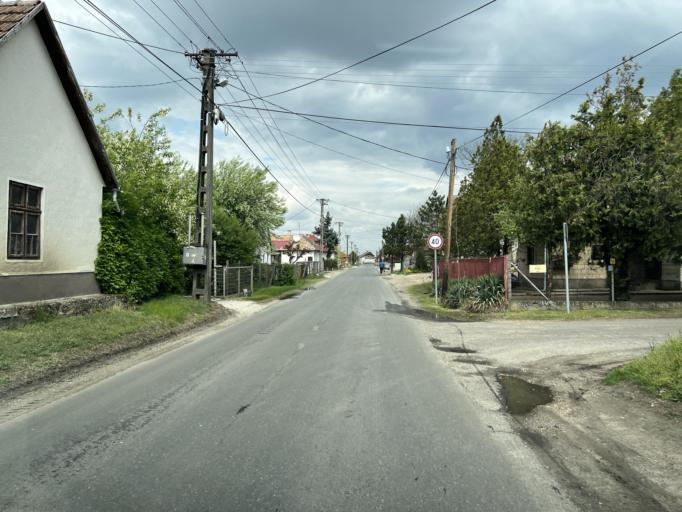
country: HU
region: Pest
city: Hernad
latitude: 47.1598
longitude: 19.3980
